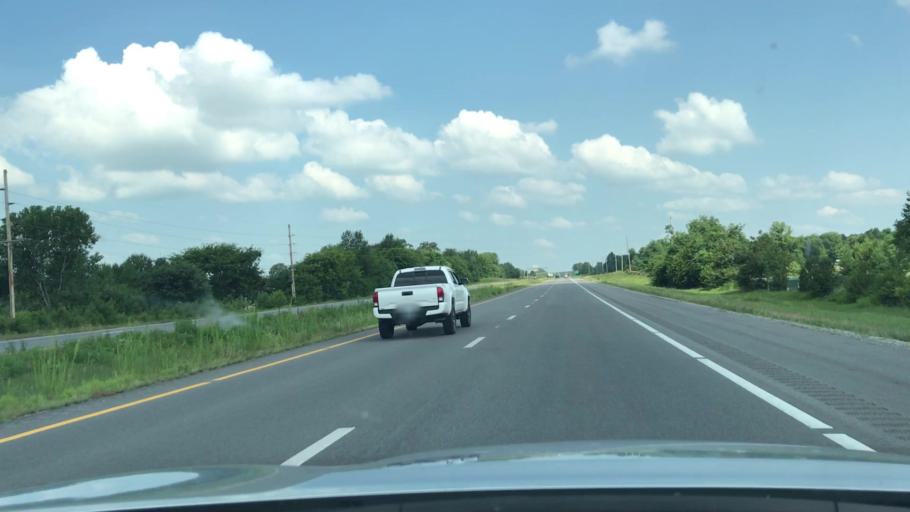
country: US
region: Kentucky
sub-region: Warren County
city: Plano
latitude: 36.9163
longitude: -86.4421
